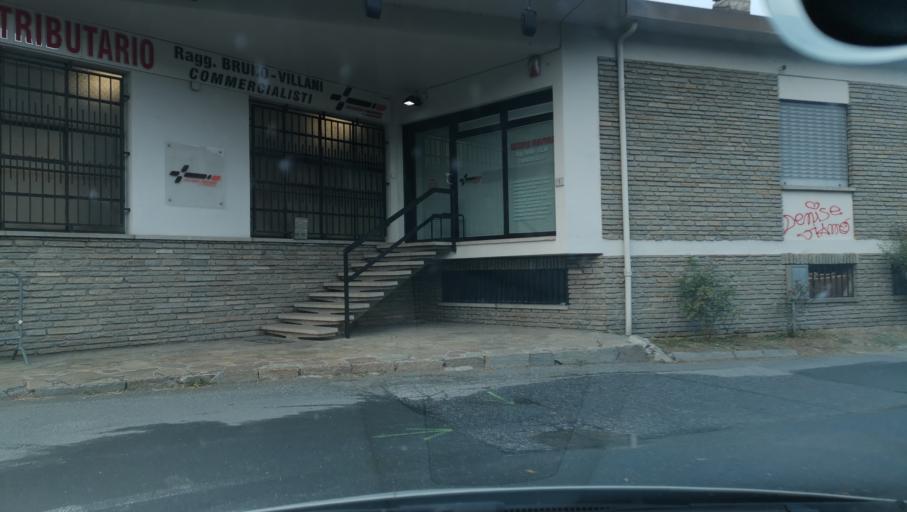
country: IT
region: Piedmont
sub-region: Provincia di Torino
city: Condove
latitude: 45.1147
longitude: 7.3128
